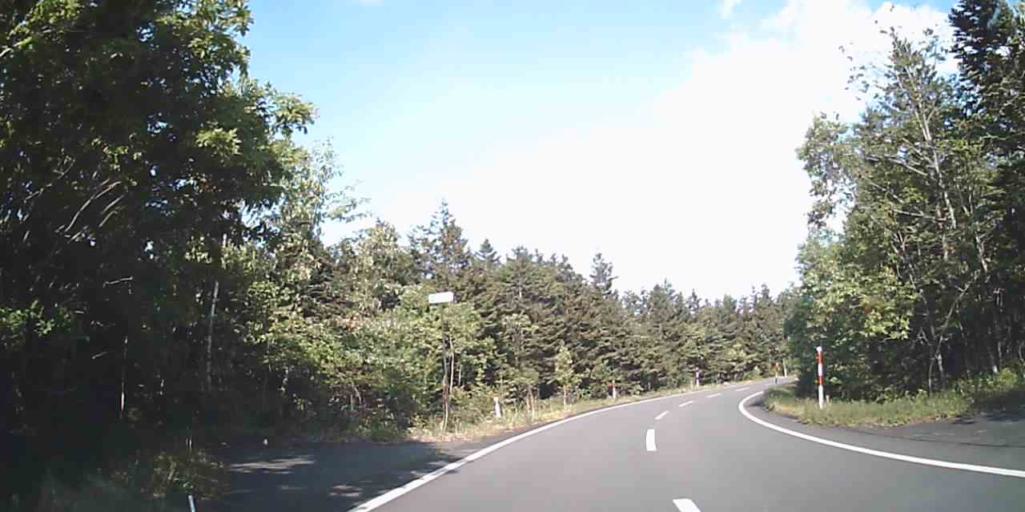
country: JP
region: Hokkaido
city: Shiraoi
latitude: 42.6886
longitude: 141.4330
